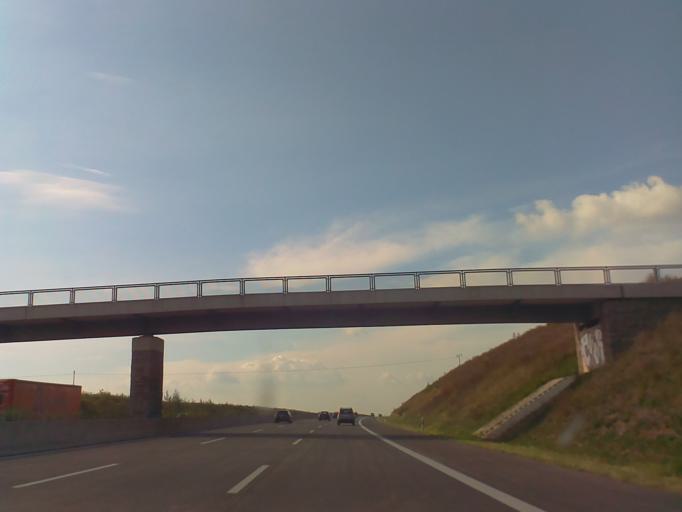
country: DE
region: Thuringia
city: Eisenach
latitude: 51.0147
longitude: 10.3391
